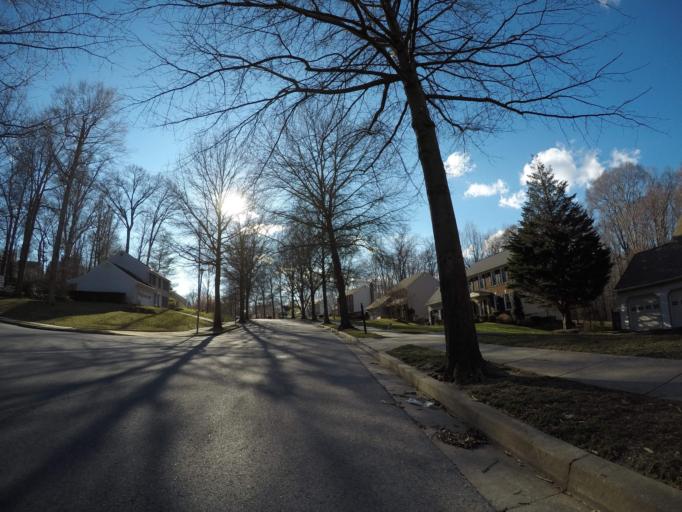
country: US
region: Maryland
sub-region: Howard County
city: Ellicott City
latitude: 39.2586
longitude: -76.8049
